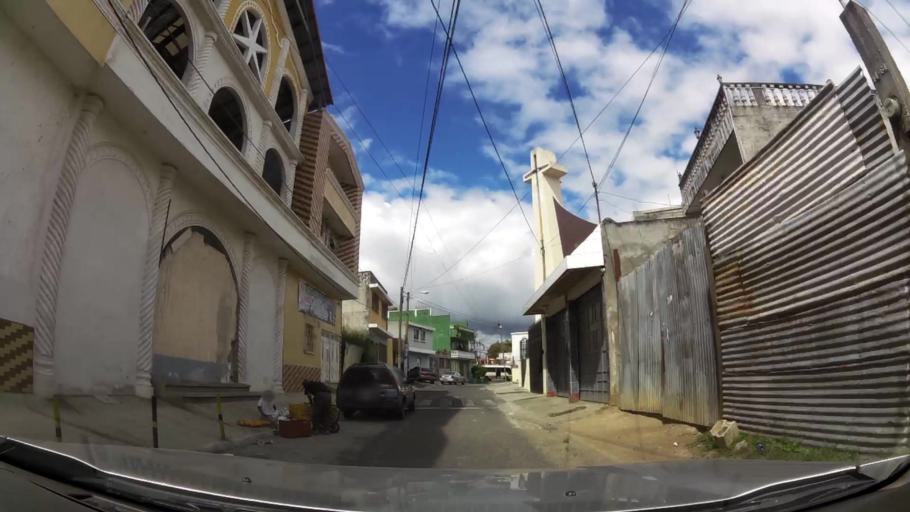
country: GT
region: Guatemala
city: Chinautla
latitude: 14.6824
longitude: -90.5418
